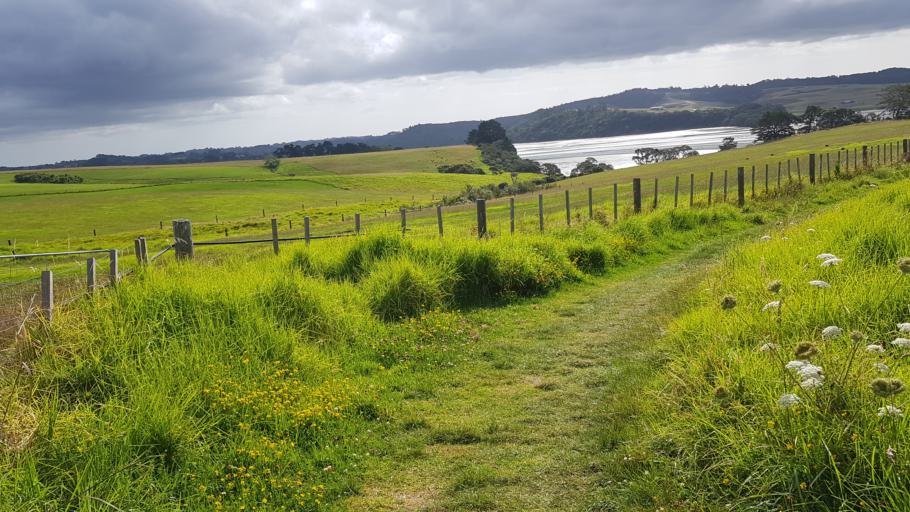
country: NZ
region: Auckland
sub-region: Auckland
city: Rothesay Bay
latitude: -36.6633
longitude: 174.7453
